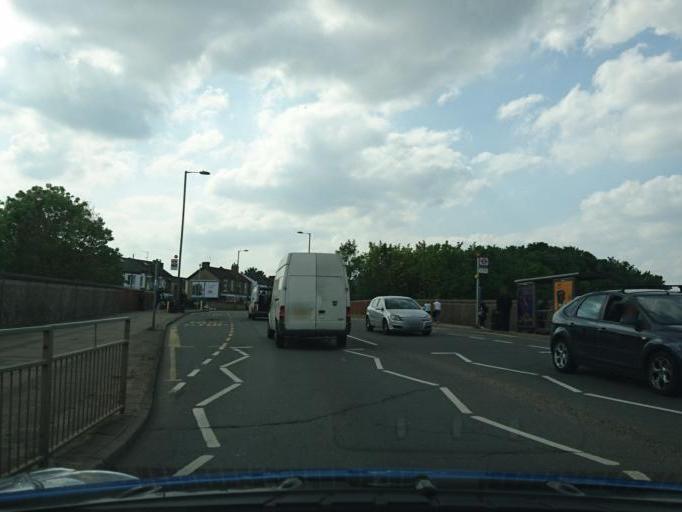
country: GB
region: England
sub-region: Greater London
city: Wood Green
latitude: 51.6227
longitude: -0.1512
